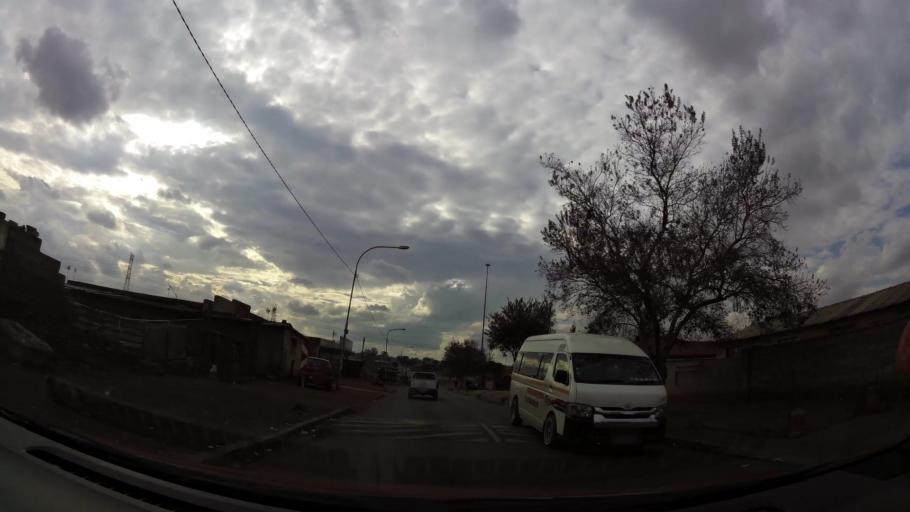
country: ZA
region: Gauteng
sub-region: City of Johannesburg Metropolitan Municipality
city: Soweto
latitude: -26.2479
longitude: 27.8410
